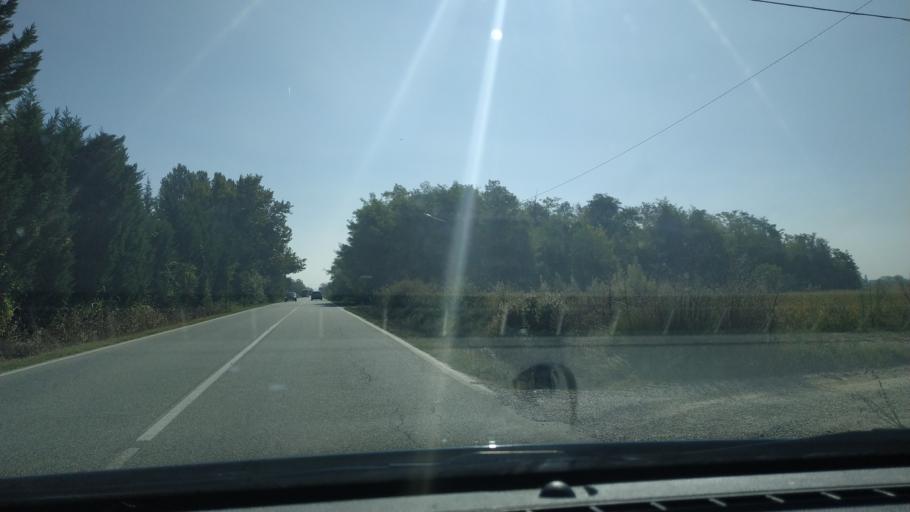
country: IT
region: Piedmont
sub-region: Provincia di Alessandria
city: Borgo San Martino
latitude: 45.1138
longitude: 8.5037
